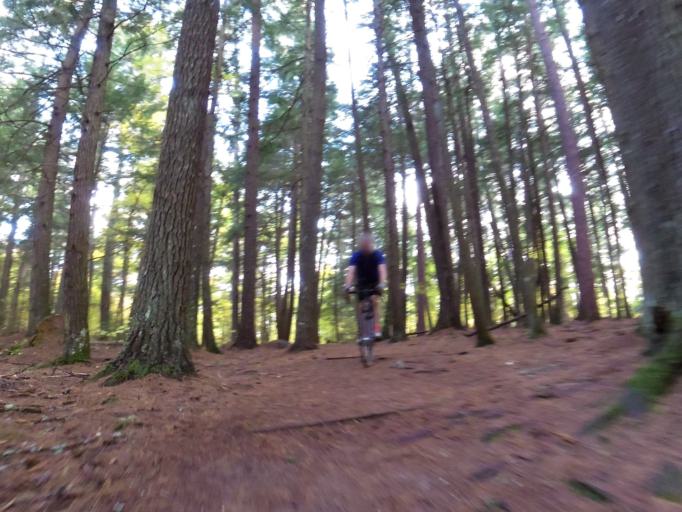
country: CA
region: Ontario
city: Deep River
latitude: 45.8878
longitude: -77.6368
